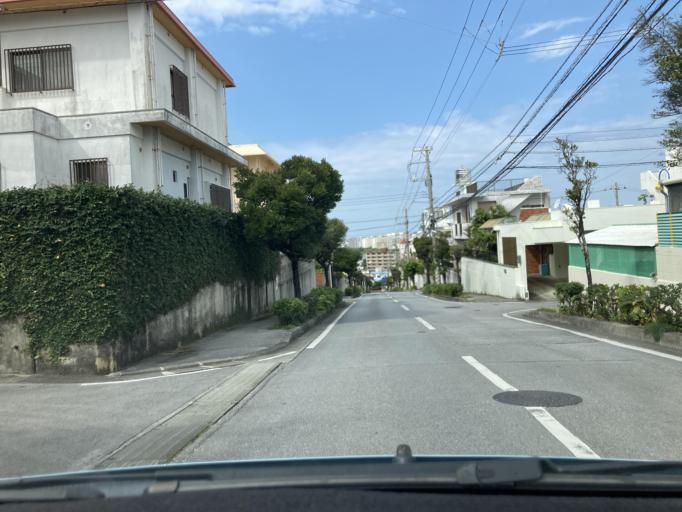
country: JP
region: Okinawa
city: Tomigusuku
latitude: 26.1881
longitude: 127.6950
